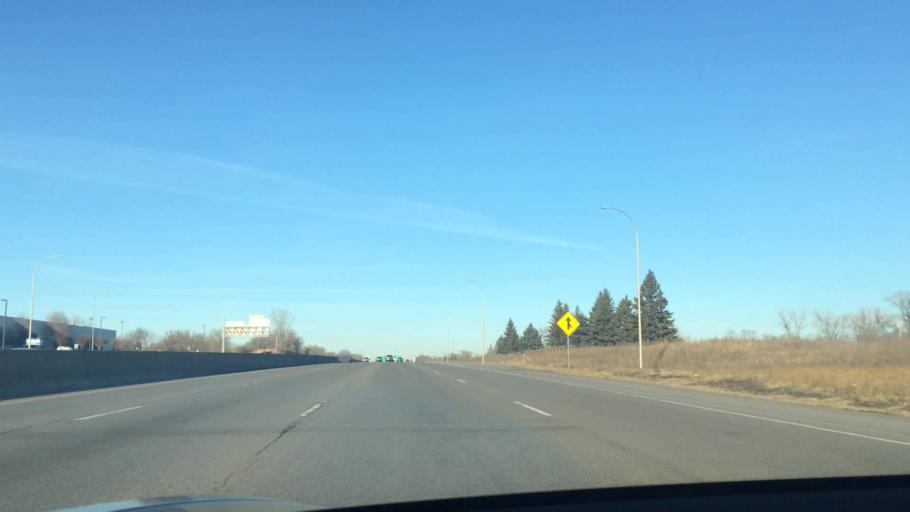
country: US
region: Minnesota
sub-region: Ramsey County
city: Mounds View
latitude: 45.0973
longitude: -93.1881
